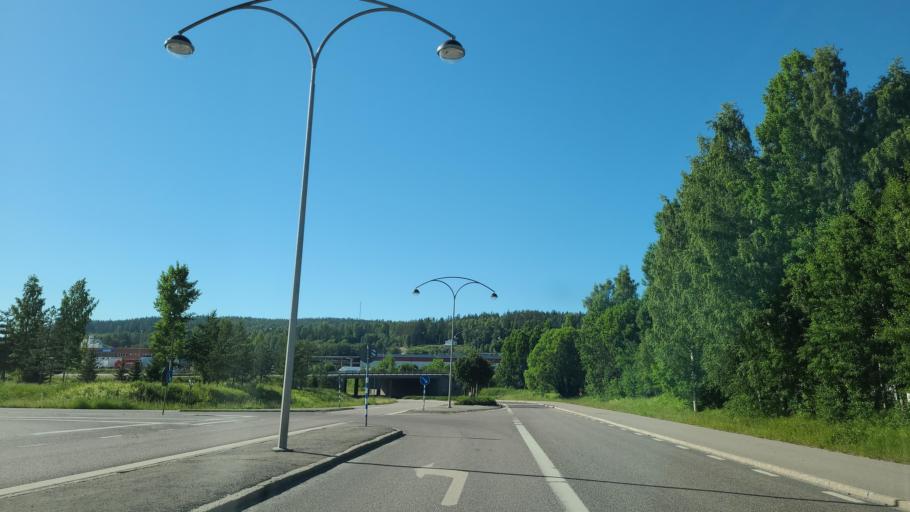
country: SE
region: Vaesternorrland
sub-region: Sundsvalls Kommun
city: Sundsbruk
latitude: 62.4474
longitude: 17.3442
